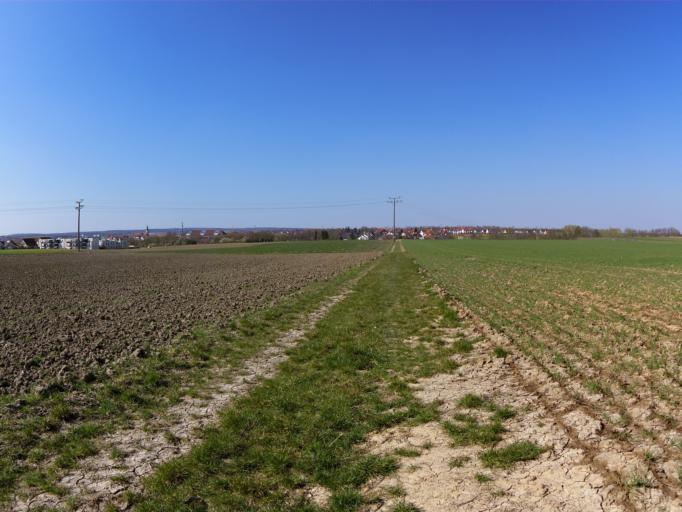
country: DE
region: Bavaria
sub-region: Regierungsbezirk Unterfranken
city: Kurnach
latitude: 49.8402
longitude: 10.0527
